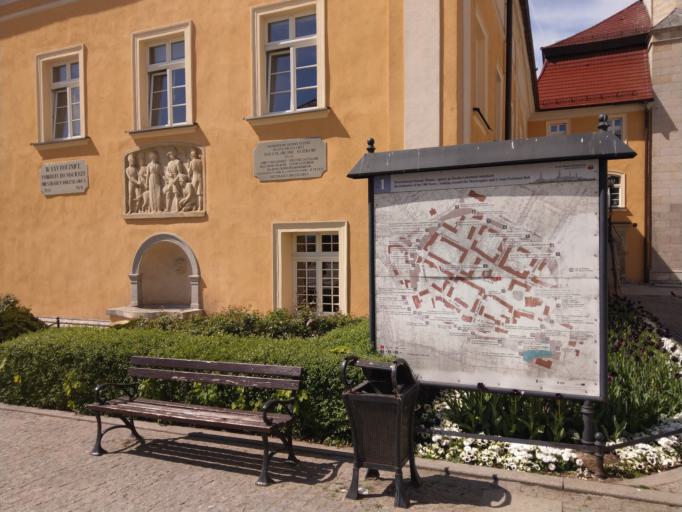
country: PL
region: Lower Silesian Voivodeship
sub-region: Powiat boleslawiecki
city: Boleslawiec
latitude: 51.2630
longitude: 15.5653
